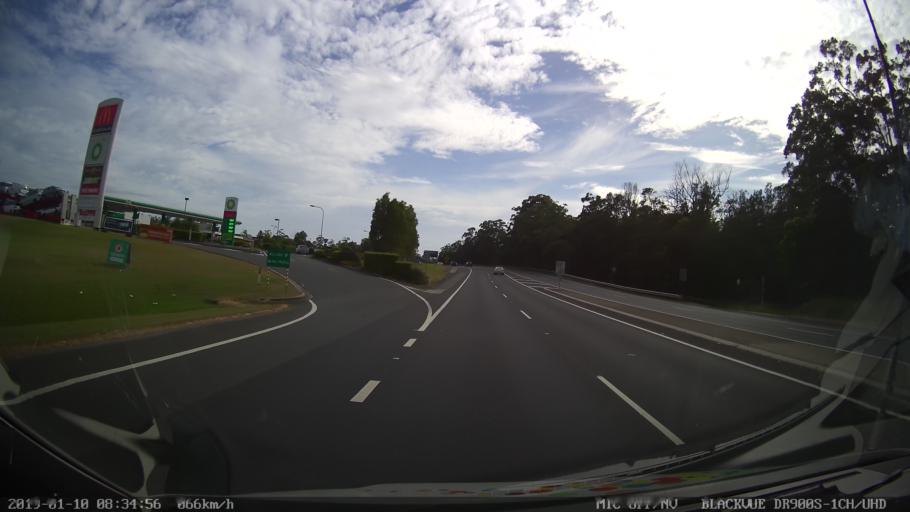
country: AU
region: New South Wales
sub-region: Coffs Harbour
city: Boambee
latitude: -30.3194
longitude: 153.0882
